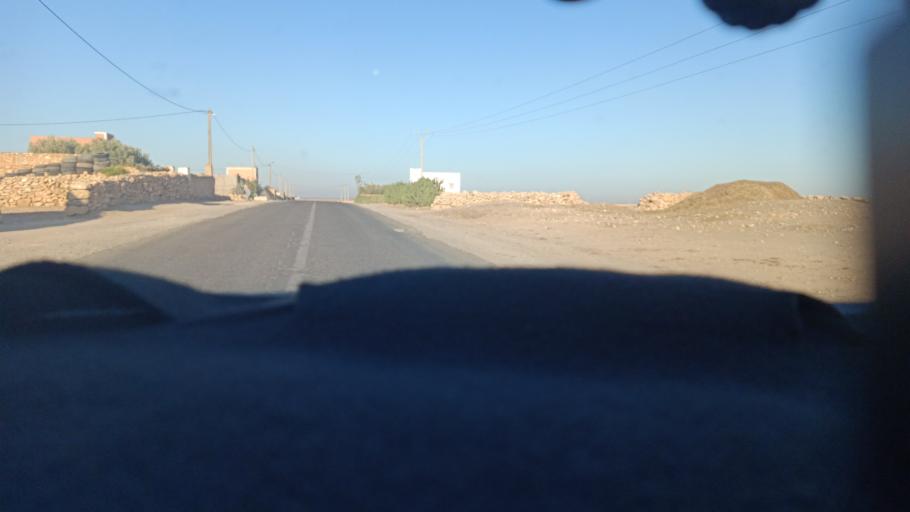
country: MA
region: Doukkala-Abda
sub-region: Safi
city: Youssoufia
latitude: 32.3707
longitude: -8.6767
